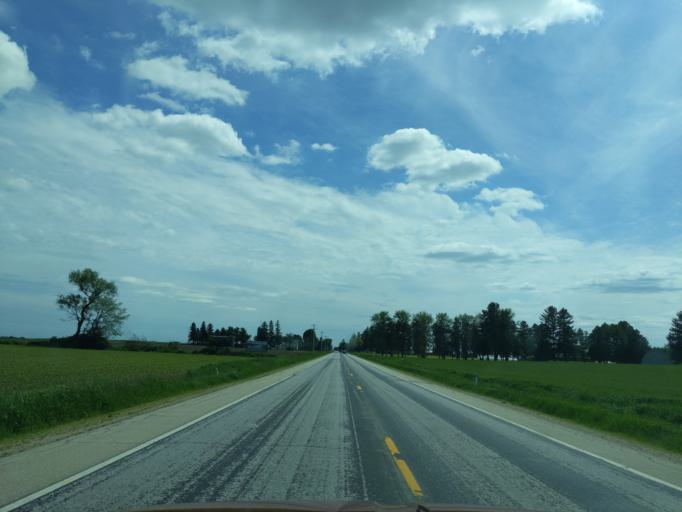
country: US
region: Wisconsin
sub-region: Dane County
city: De Forest
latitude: 43.3186
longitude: -89.3254
